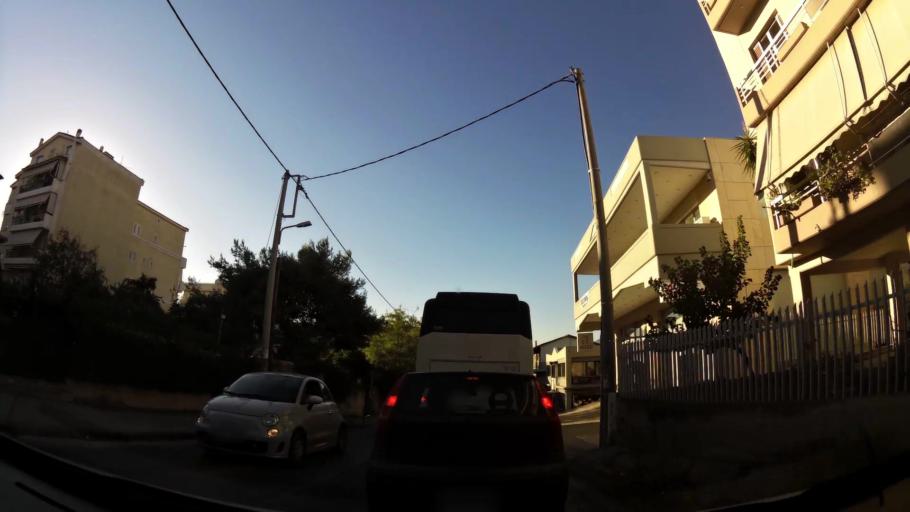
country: GR
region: Attica
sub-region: Nomarchia Athinas
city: Lykovrysi
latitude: 38.0639
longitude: 23.7771
